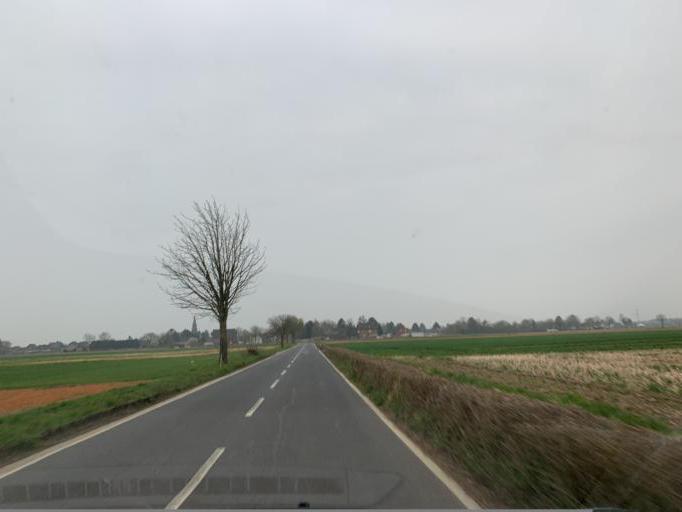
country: DE
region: North Rhine-Westphalia
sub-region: Regierungsbezirk Koln
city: Elsdorf
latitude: 50.8859
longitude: 6.6070
